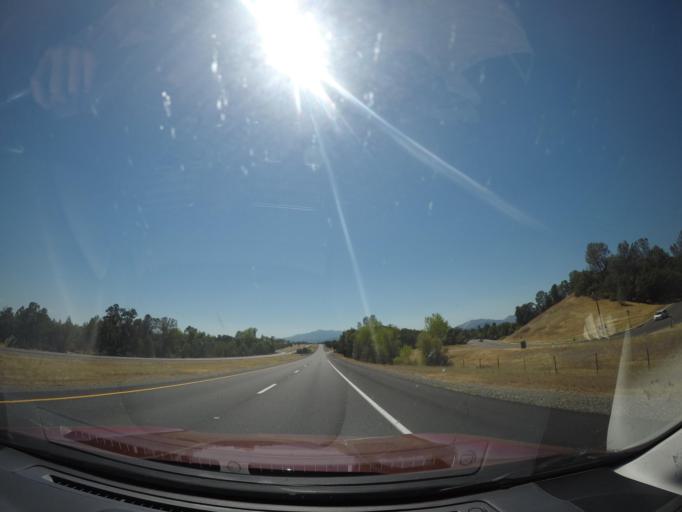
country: US
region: California
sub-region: Shasta County
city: Redding
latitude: 40.6160
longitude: -122.3435
